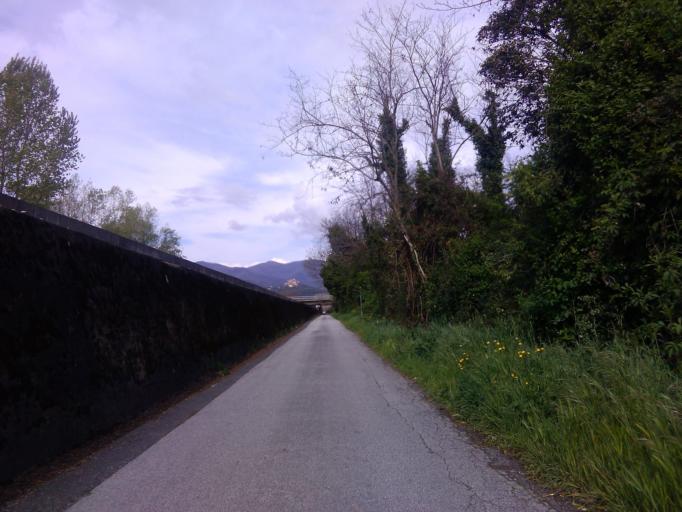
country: IT
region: Tuscany
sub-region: Provincia di Massa-Carrara
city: Marina di Carrara
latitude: 44.0532
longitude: 10.0246
